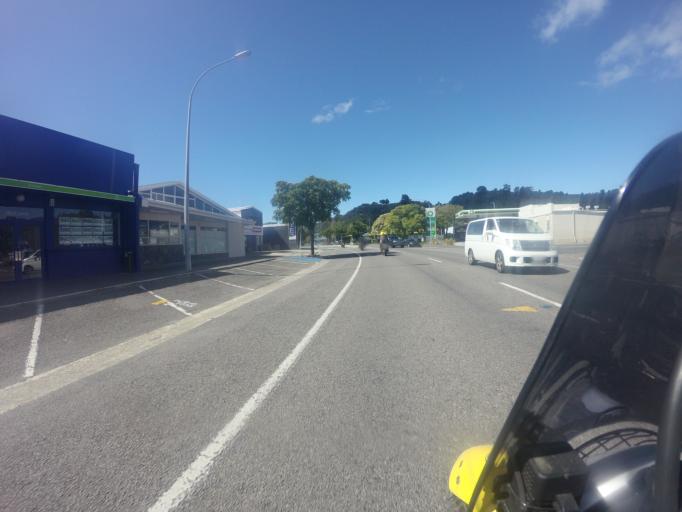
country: NZ
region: Bay of Plenty
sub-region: Whakatane District
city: Whakatane
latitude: -37.9536
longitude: 176.9901
